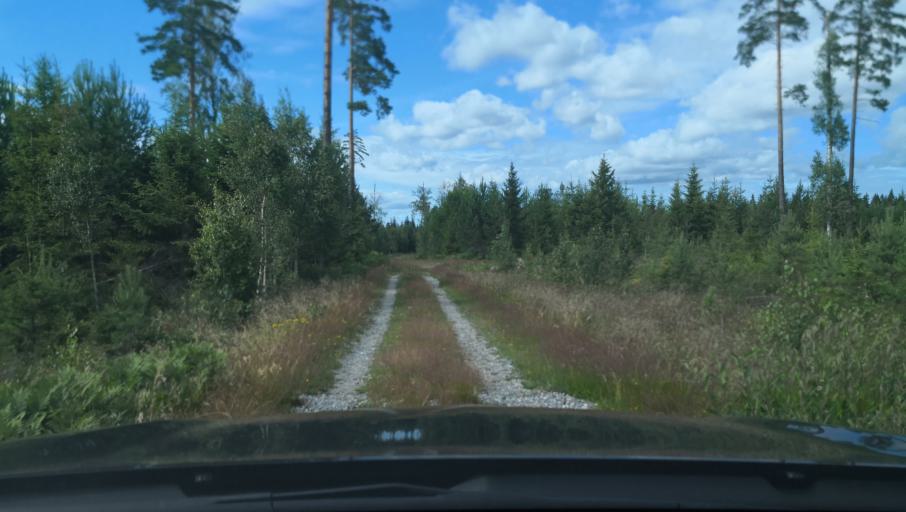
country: SE
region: Vaestmanland
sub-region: Surahammars Kommun
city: Surahammar
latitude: 59.6516
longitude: 16.0842
